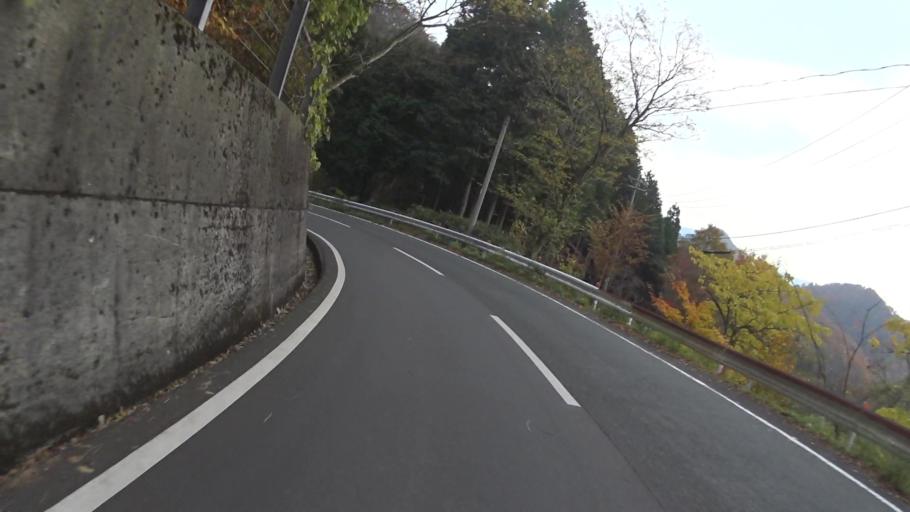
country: JP
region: Kyoto
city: Maizuru
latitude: 35.5412
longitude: 135.4485
